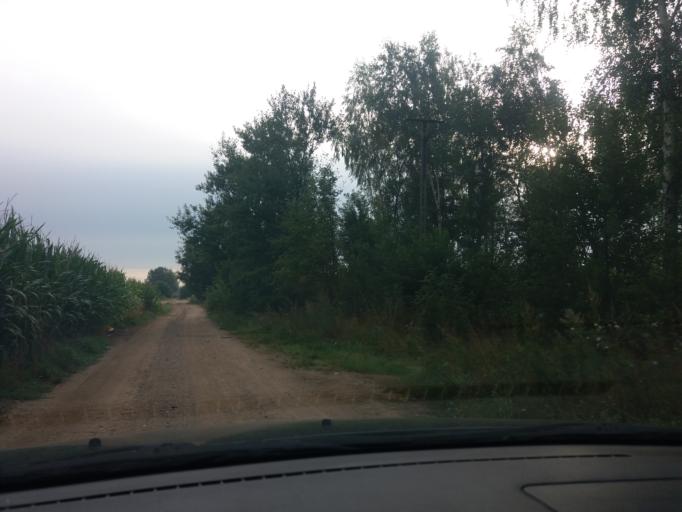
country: PL
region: Masovian Voivodeship
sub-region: Powiat mlawski
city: Wieczfnia Koscielna
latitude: 53.2013
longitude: 20.4402
